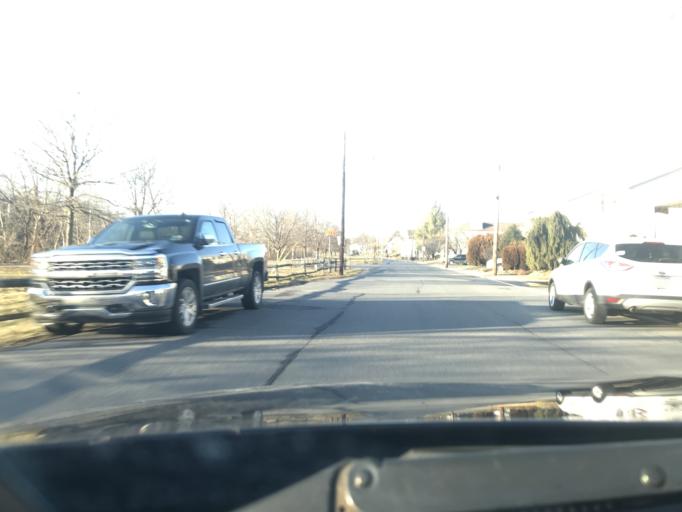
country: US
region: Pennsylvania
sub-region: Northampton County
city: Northampton
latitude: 40.6826
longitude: -75.4986
